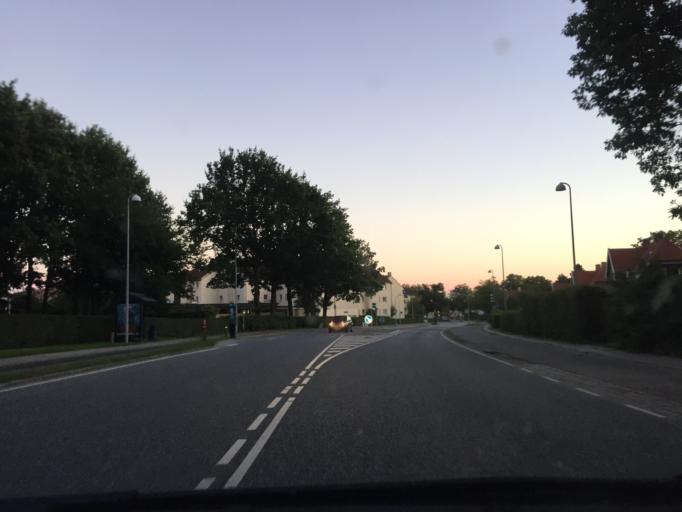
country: DK
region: Capital Region
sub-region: Lyngby-Tarbaek Kommune
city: Kongens Lyngby
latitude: 55.7812
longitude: 12.5105
